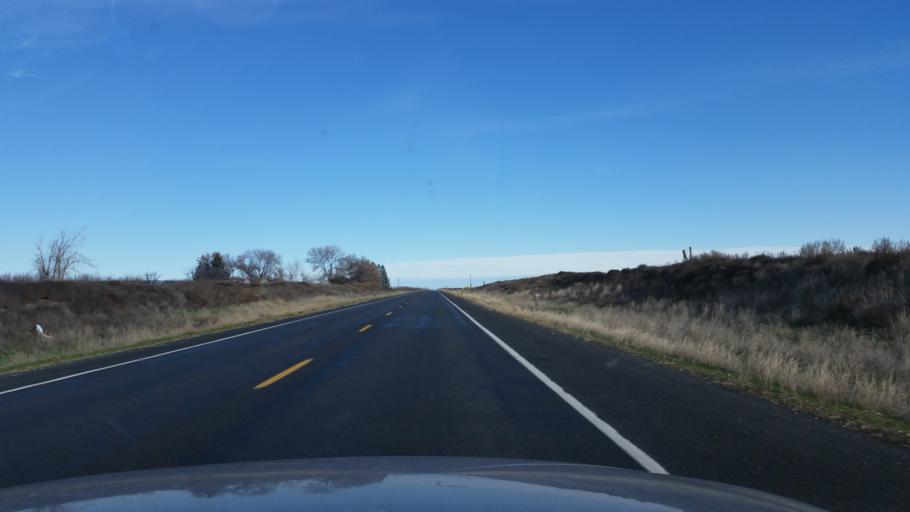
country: US
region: Washington
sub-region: Grant County
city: Quincy
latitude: 47.1659
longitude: -119.7317
